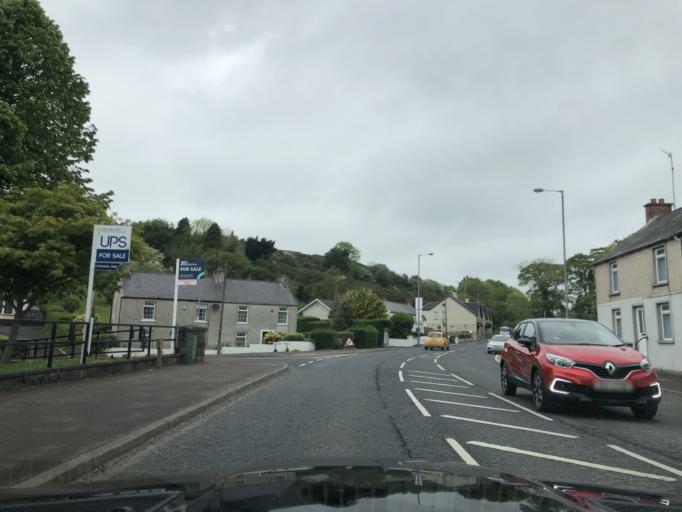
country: GB
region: Northern Ireland
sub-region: Down District
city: Downpatrick
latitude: 54.3353
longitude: -5.7167
